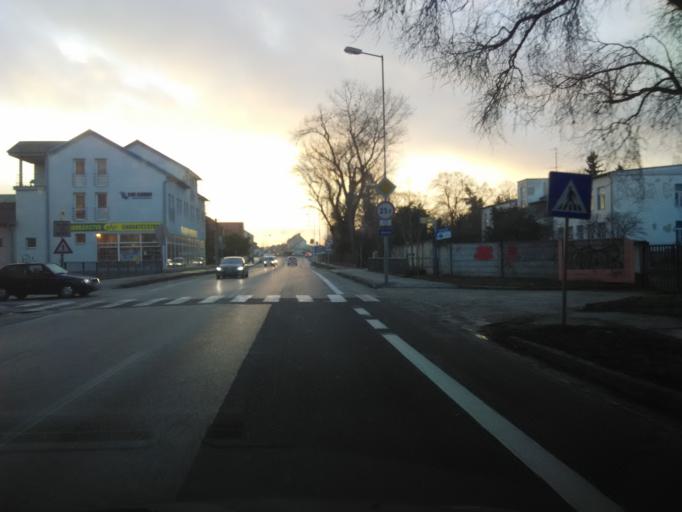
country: SK
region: Trnavsky
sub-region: Okres Trnava
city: Trnava
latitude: 48.3671
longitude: 17.5912
